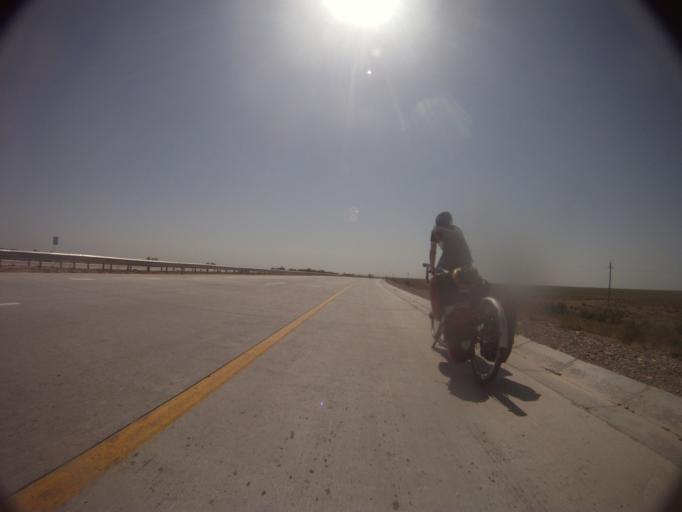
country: KZ
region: Ongtustik Qazaqstan
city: Khantaghy
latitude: 43.1229
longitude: 68.6000
